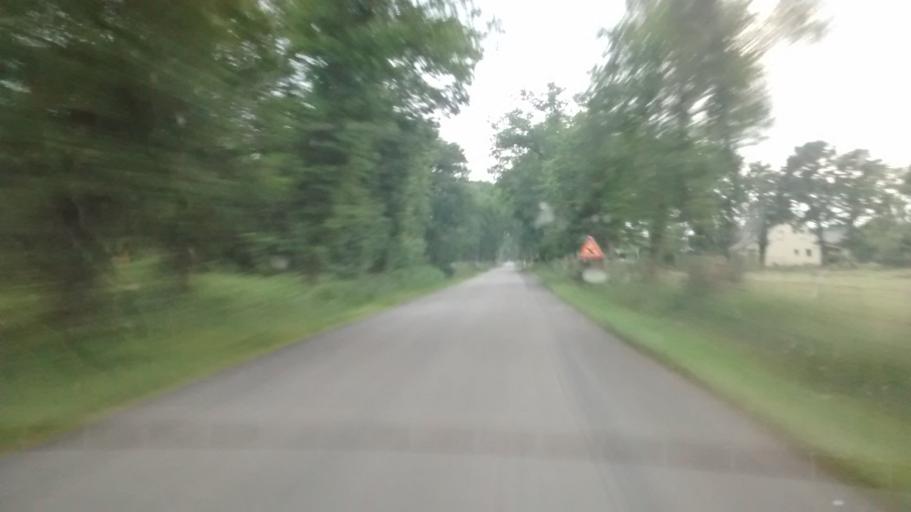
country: FR
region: Brittany
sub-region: Departement du Morbihan
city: Pleucadeuc
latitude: 47.7359
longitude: -2.3438
